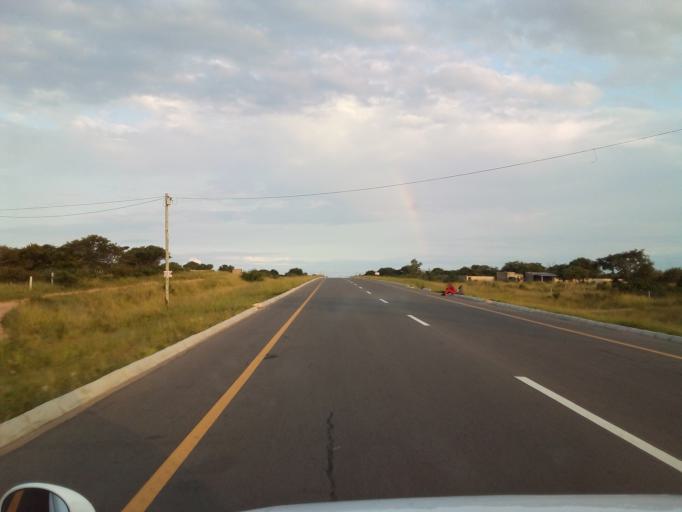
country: MZ
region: Maputo City
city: Maputo
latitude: -26.0641
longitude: 32.5982
